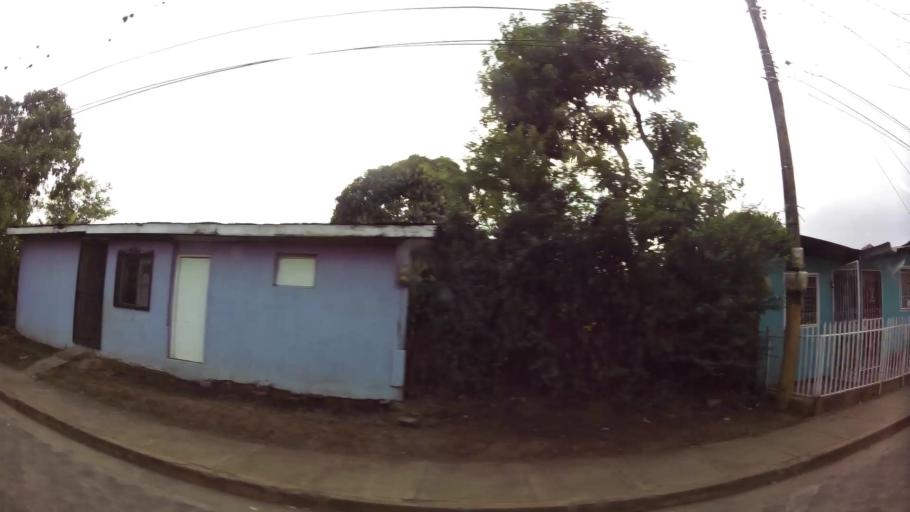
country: NI
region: Masaya
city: Masaya
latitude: 11.9809
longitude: -86.0992
